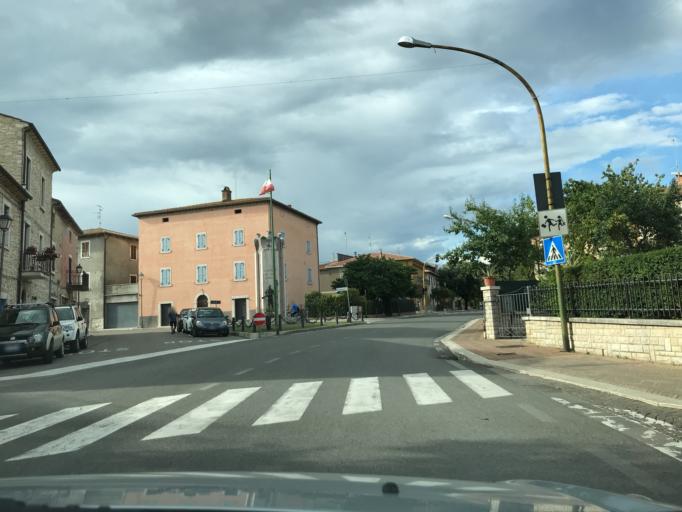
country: IT
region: Umbria
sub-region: Provincia di Terni
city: Guardea
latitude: 42.6247
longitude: 12.2960
